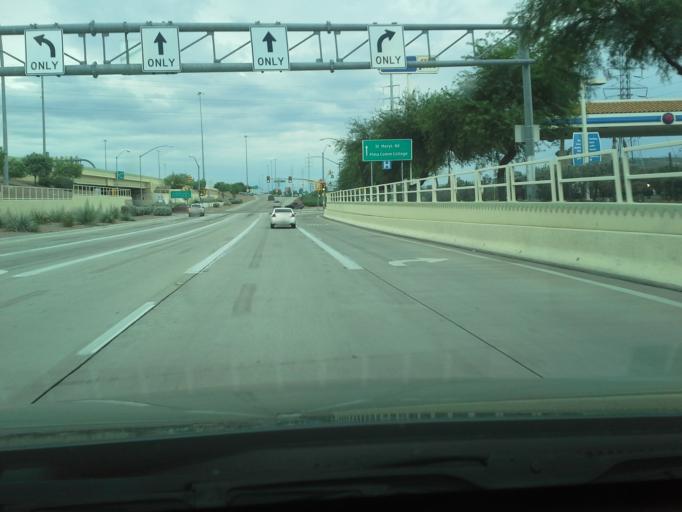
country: US
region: Arizona
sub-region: Pima County
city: South Tucson
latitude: 32.2368
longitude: -110.9848
